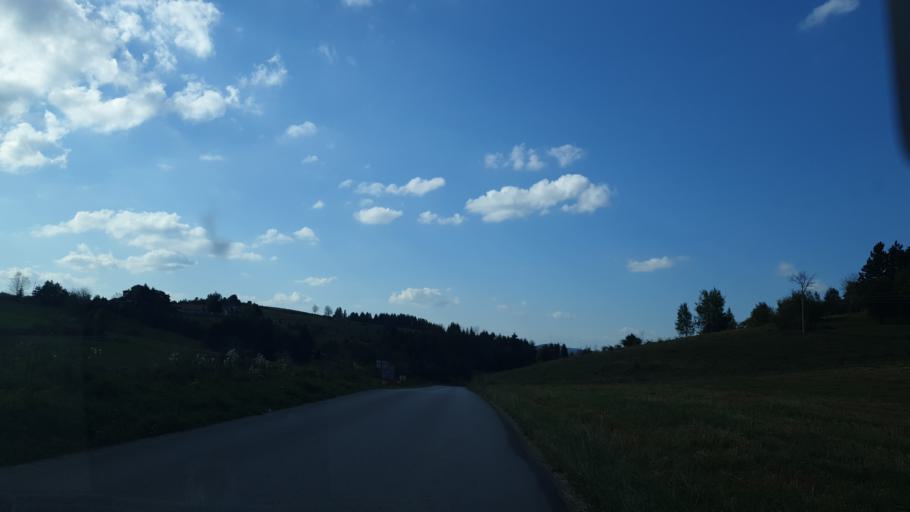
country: RS
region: Central Serbia
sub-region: Zlatiborski Okrug
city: Nova Varos
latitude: 43.4265
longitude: 19.8764
